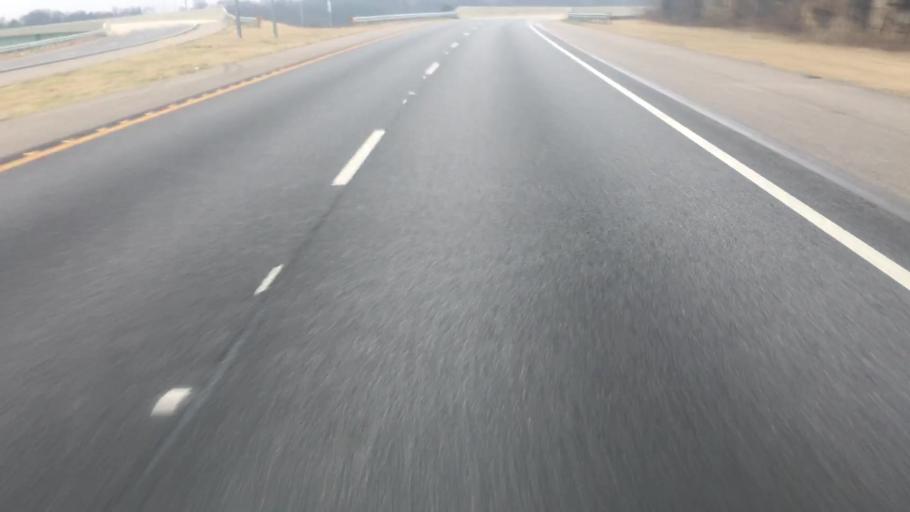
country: US
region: Alabama
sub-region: Jefferson County
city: Fultondale
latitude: 33.5748
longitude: -86.8201
